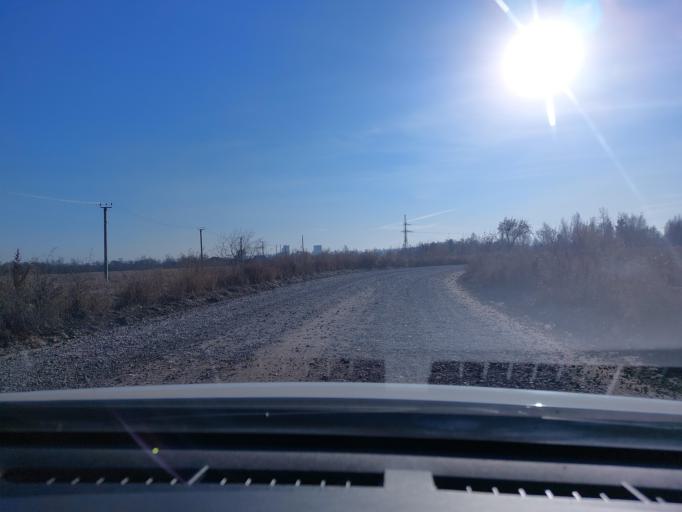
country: RU
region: Irkutsk
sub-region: Irkutskiy Rayon
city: Irkutsk
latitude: 52.3044
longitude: 104.2764
